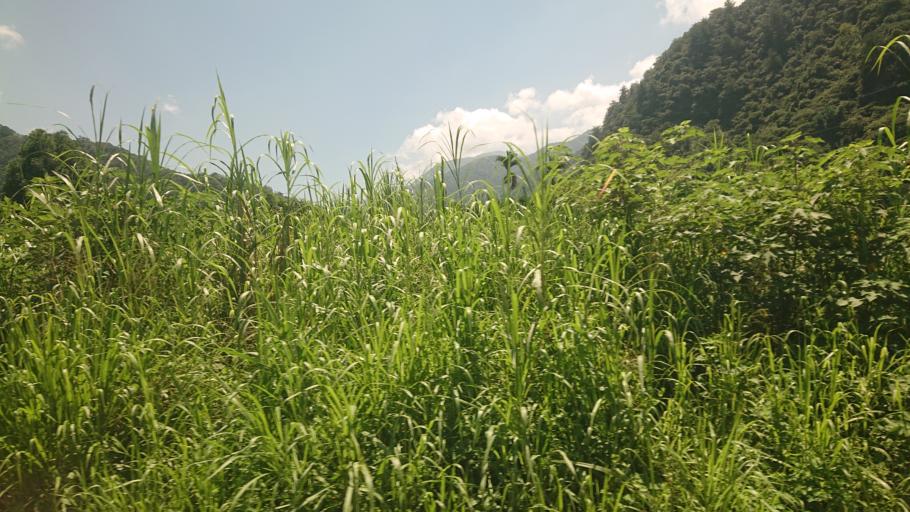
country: TW
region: Taiwan
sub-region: Nantou
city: Puli
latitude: 24.0640
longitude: 120.9531
